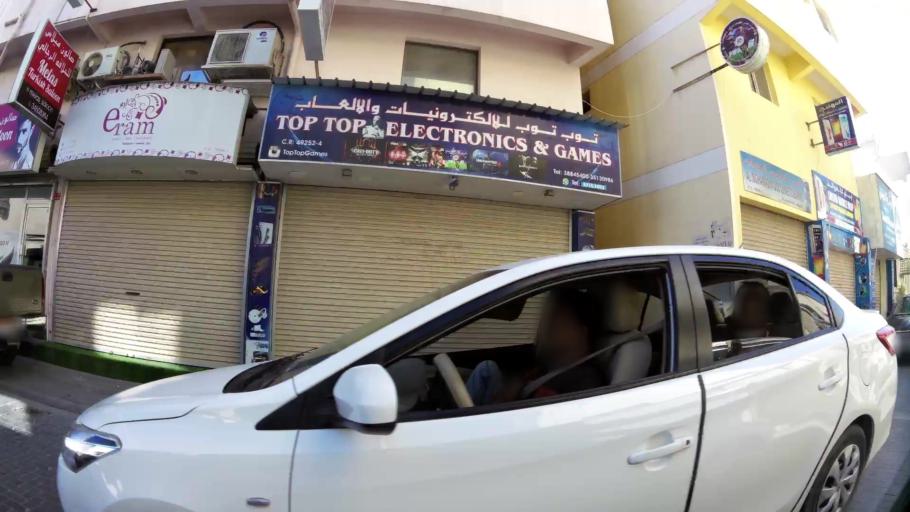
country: BH
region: Muharraq
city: Al Hadd
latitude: 26.2420
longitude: 50.6548
